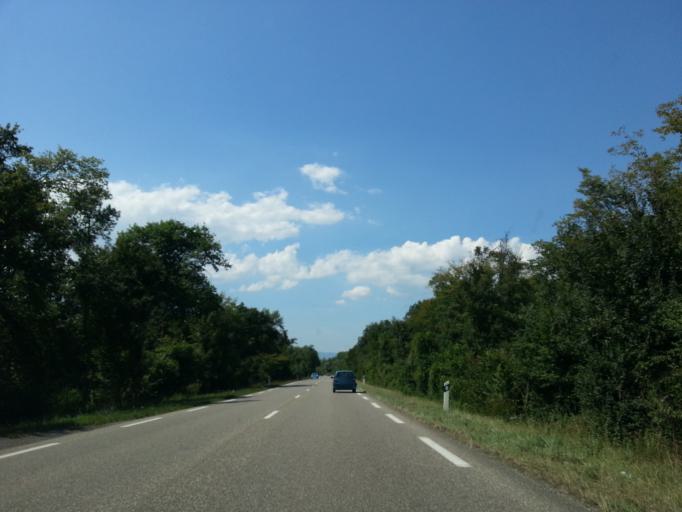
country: FR
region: Alsace
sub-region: Departement du Haut-Rhin
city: Widensolen
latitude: 48.0517
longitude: 7.4523
